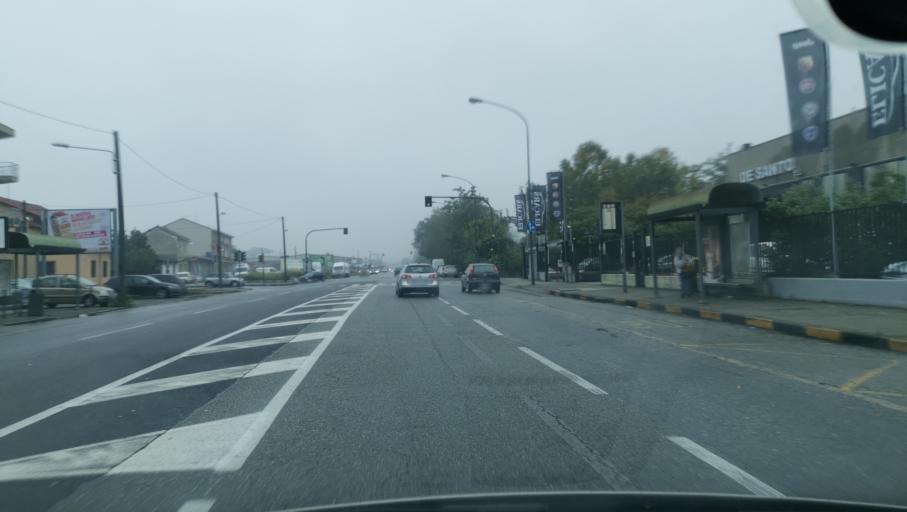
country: IT
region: Piedmont
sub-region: Provincia di Torino
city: Turin
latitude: 45.1099
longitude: 7.6811
